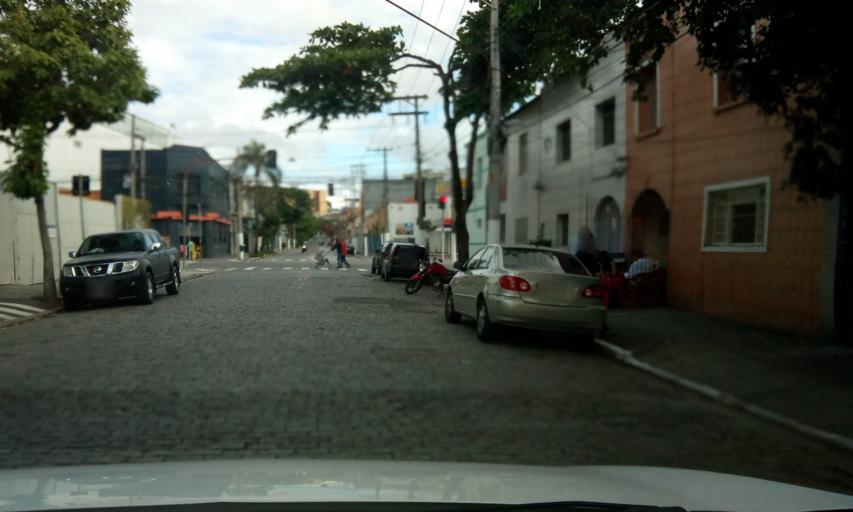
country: BR
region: Sao Paulo
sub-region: Sao Paulo
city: Sao Paulo
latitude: -23.5444
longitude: -46.5881
